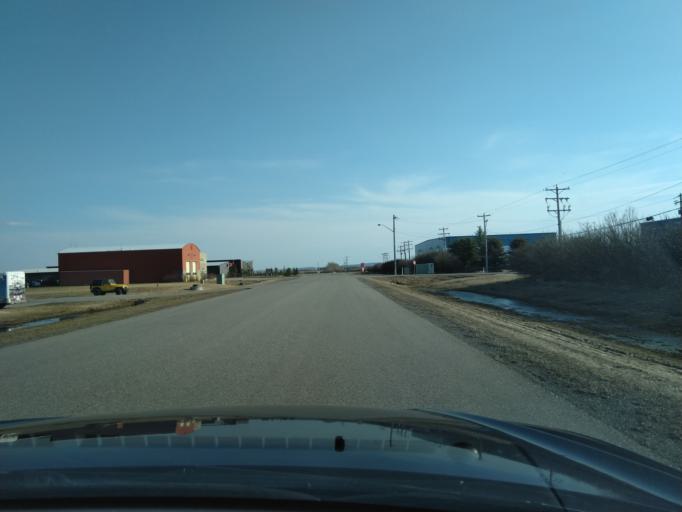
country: CA
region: Alberta
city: Cochrane
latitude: 51.0992
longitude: -114.3738
